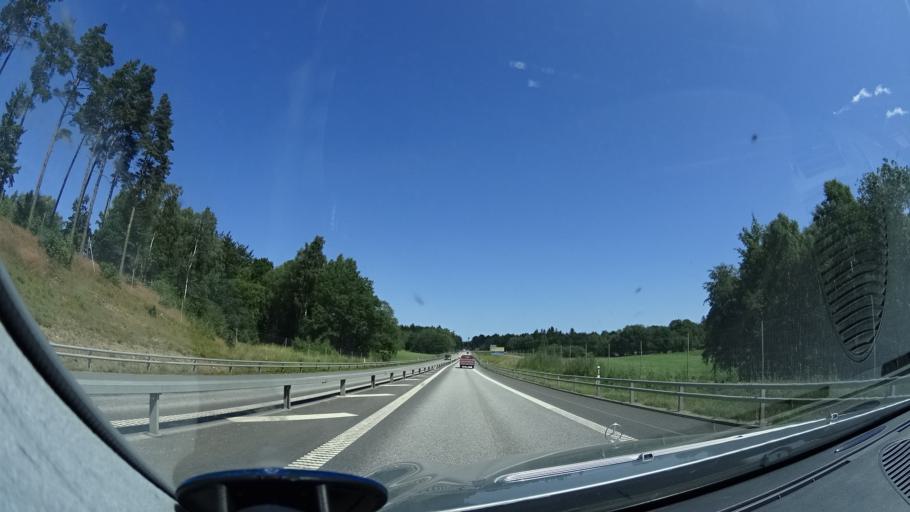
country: SE
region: Skane
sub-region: Horby Kommun
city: Hoerby
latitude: 55.9215
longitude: 13.7881
